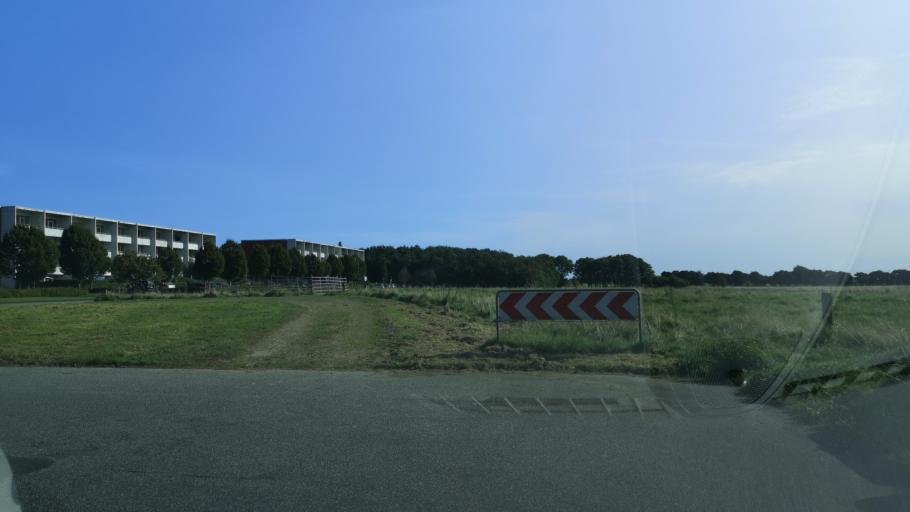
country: DK
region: Central Jutland
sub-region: Herning Kommune
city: Herning
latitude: 56.1640
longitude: 8.9796
